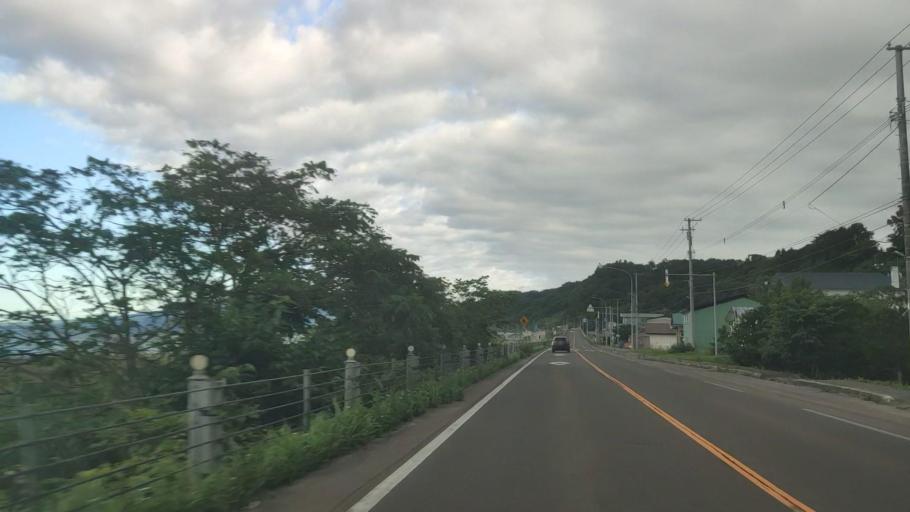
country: JP
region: Hokkaido
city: Nanae
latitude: 42.1317
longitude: 140.5111
